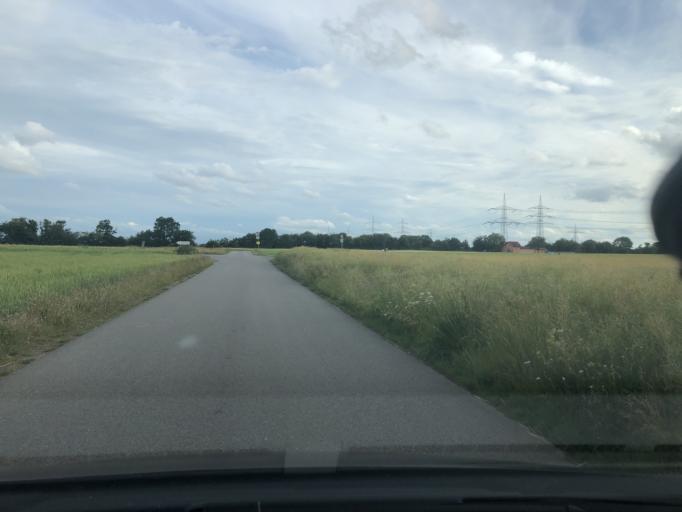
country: DE
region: Baden-Wuerttemberg
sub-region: Karlsruhe Region
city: Plankstadt
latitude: 49.3919
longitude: 8.6130
